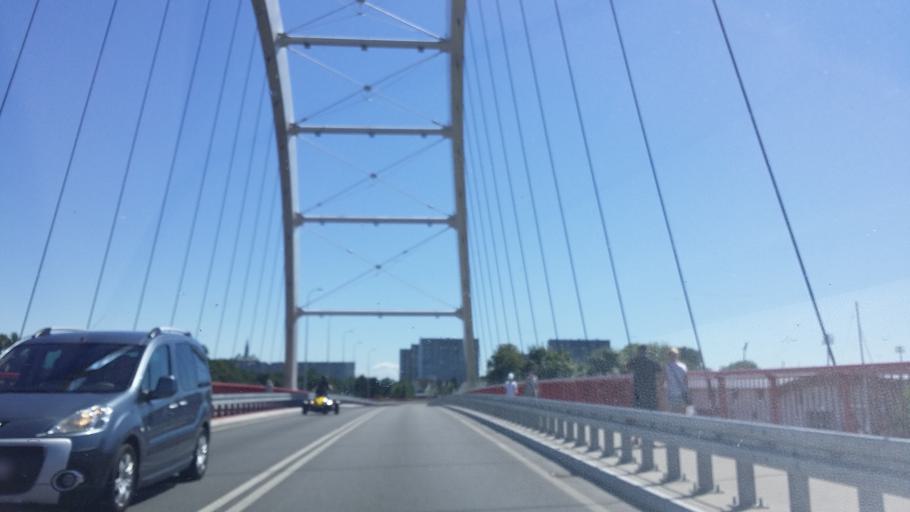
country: PL
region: West Pomeranian Voivodeship
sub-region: Powiat kolobrzeski
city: Kolobrzeg
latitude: 54.1809
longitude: 15.5587
